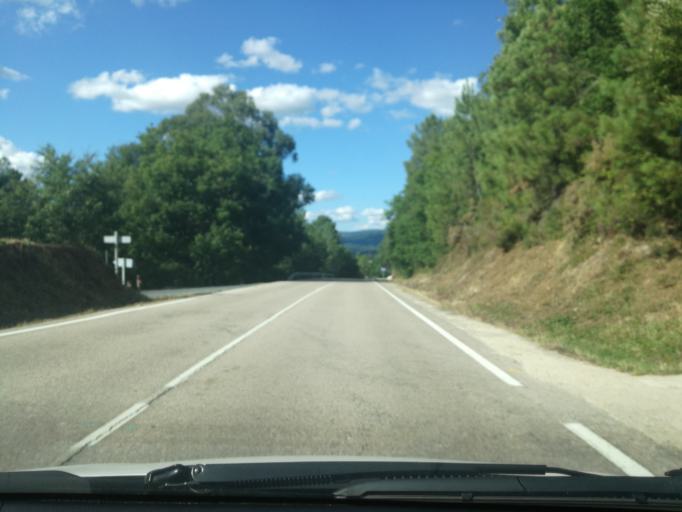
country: ES
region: Galicia
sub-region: Provincia de Ourense
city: Lobios
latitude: 41.8919
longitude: -8.0886
